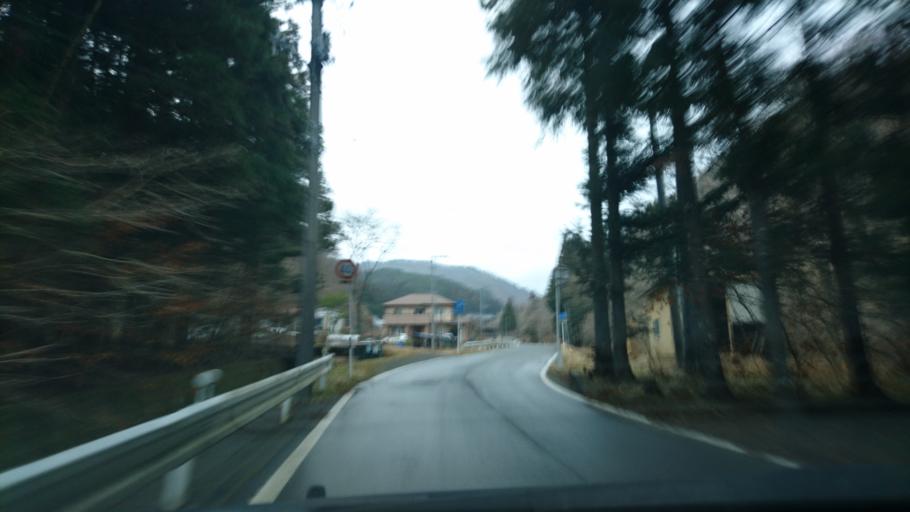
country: JP
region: Iwate
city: Ofunato
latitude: 38.9838
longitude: 141.5556
